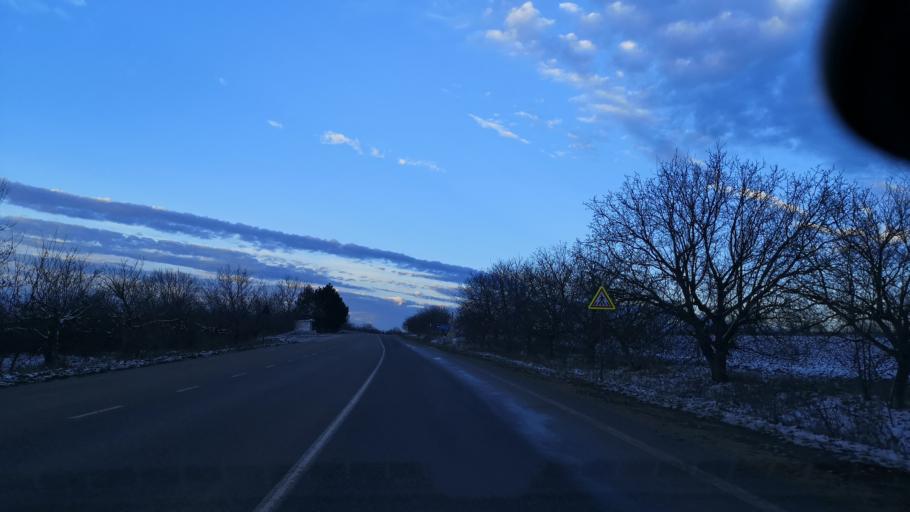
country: MD
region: Orhei
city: Orhei
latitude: 47.5507
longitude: 28.7936
